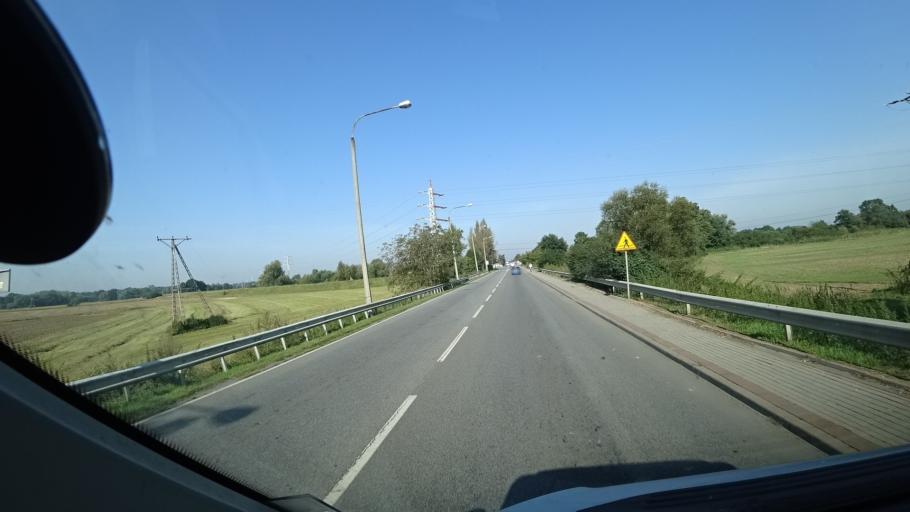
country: PL
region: Opole Voivodeship
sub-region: Powiat kedzierzynsko-kozielski
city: Kozle
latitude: 50.3382
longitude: 18.1796
